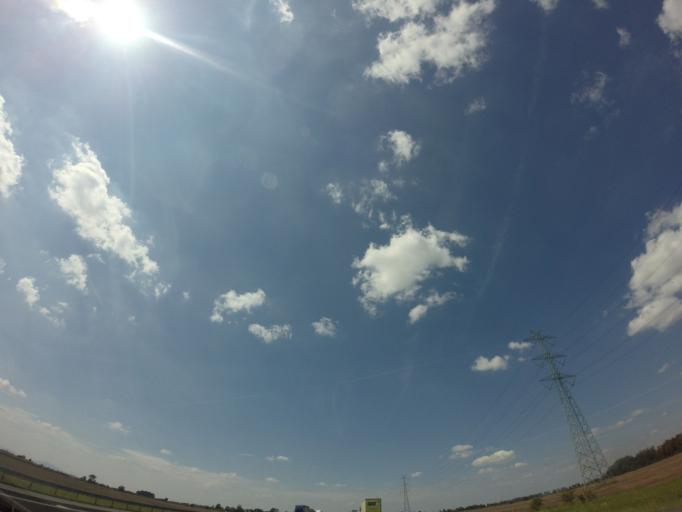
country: PL
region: Lower Silesian Voivodeship
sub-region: Powiat olawski
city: Wierzbno
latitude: 50.9004
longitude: 17.1715
